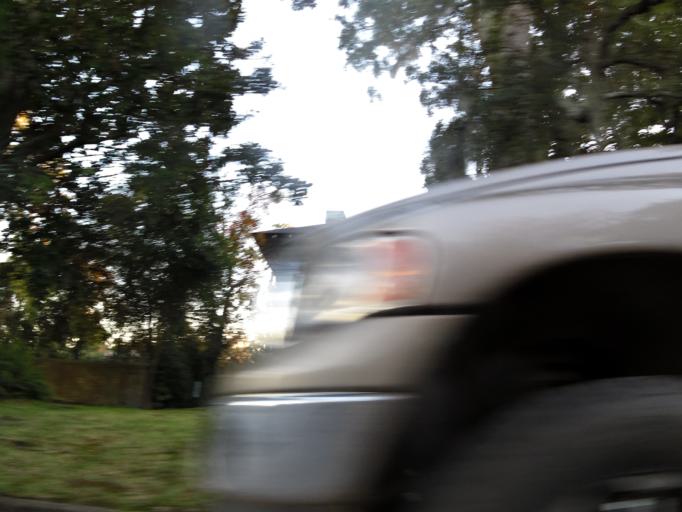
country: US
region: Florida
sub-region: Duval County
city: Jacksonville
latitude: 30.3142
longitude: -81.6843
